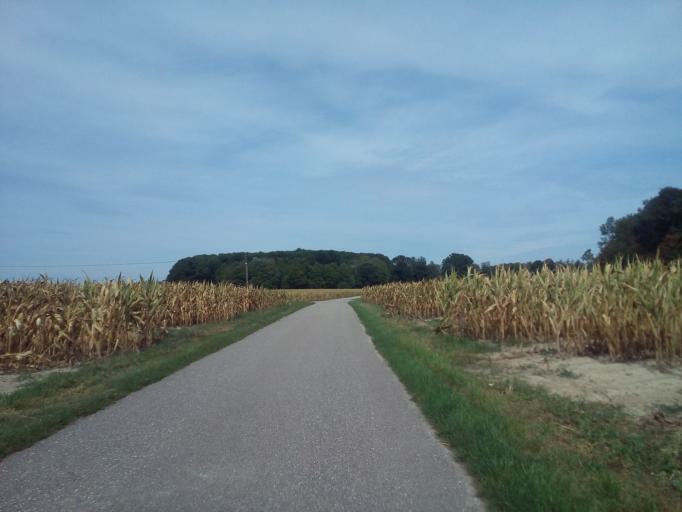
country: DE
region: Baden-Wuerttemberg
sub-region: Karlsruhe Region
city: Zell
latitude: 48.7038
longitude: 8.0454
